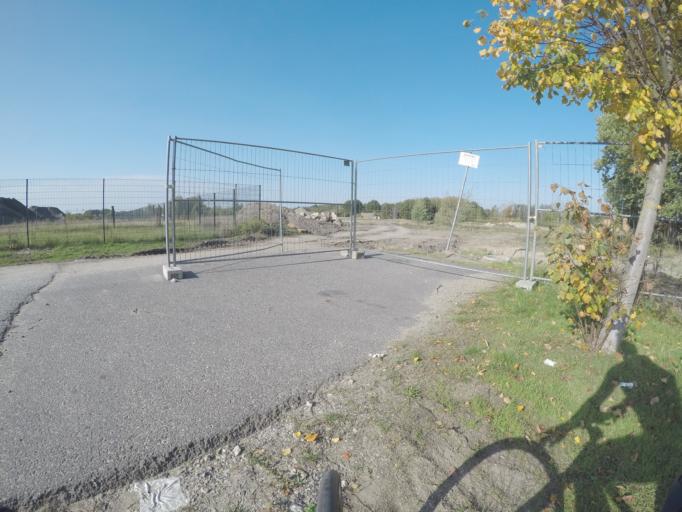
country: DE
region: Brandenburg
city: Leegebruch
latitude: 52.7343
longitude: 13.2182
